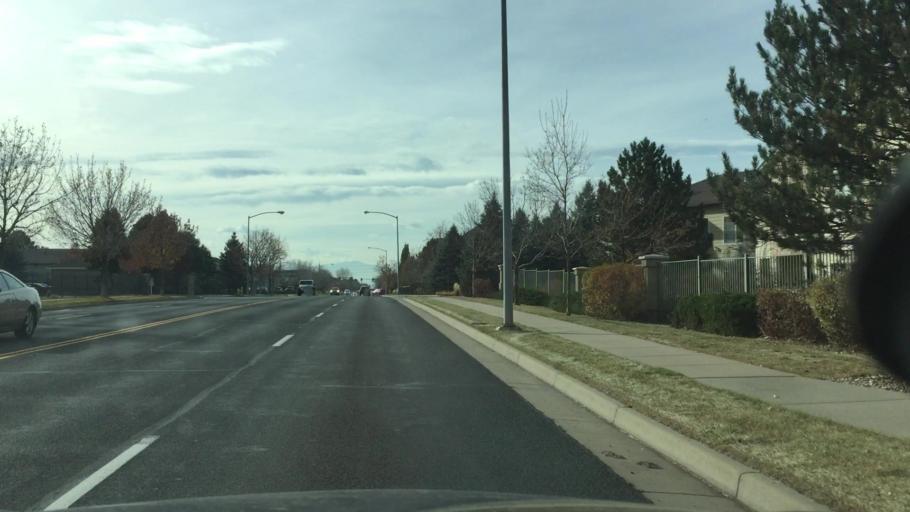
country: US
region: Colorado
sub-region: Adams County
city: Aurora
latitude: 39.6894
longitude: -104.8712
